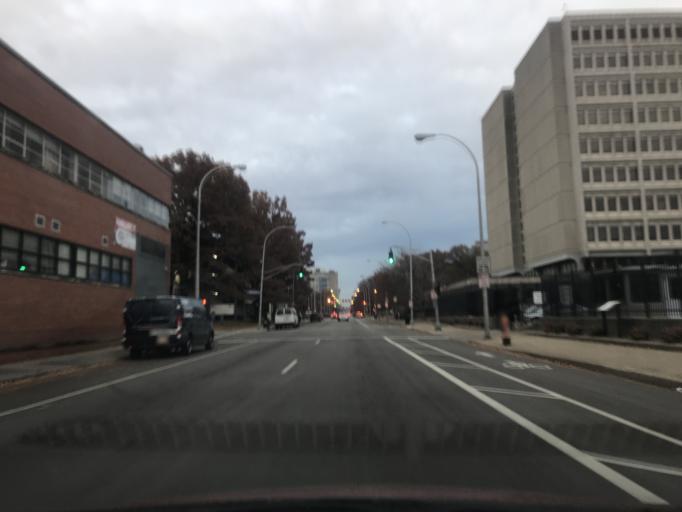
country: US
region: Kentucky
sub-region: Jefferson County
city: Louisville
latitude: 38.2478
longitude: -85.7631
